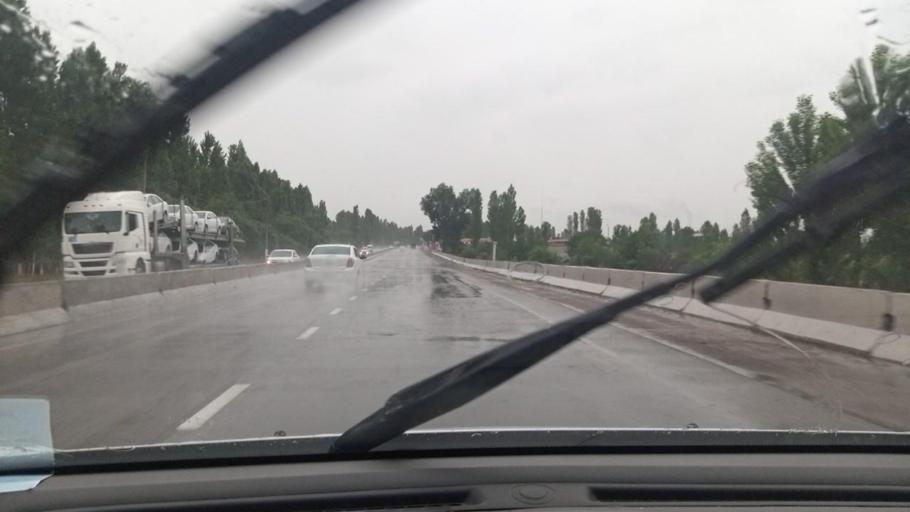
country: UZ
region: Toshkent
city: Angren
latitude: 40.9885
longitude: 70.0382
